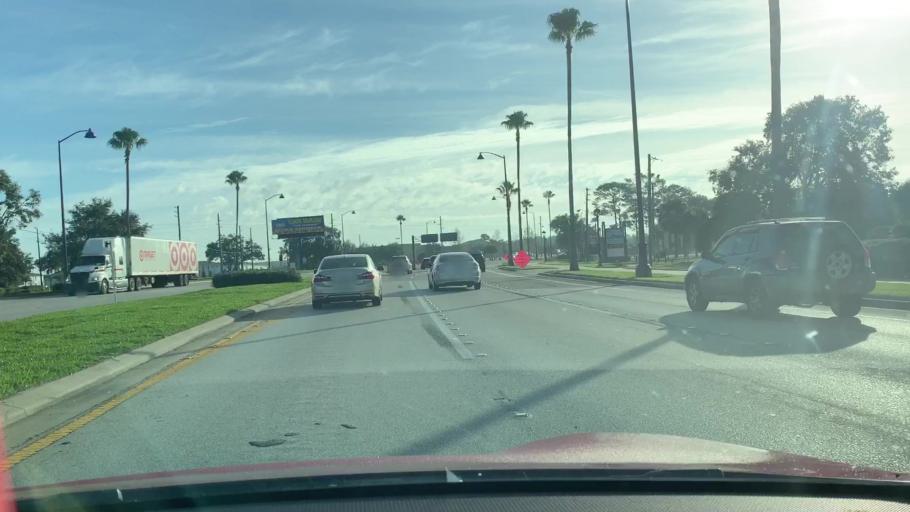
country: US
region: Florida
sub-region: Osceola County
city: Celebration
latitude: 28.3329
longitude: -81.4782
